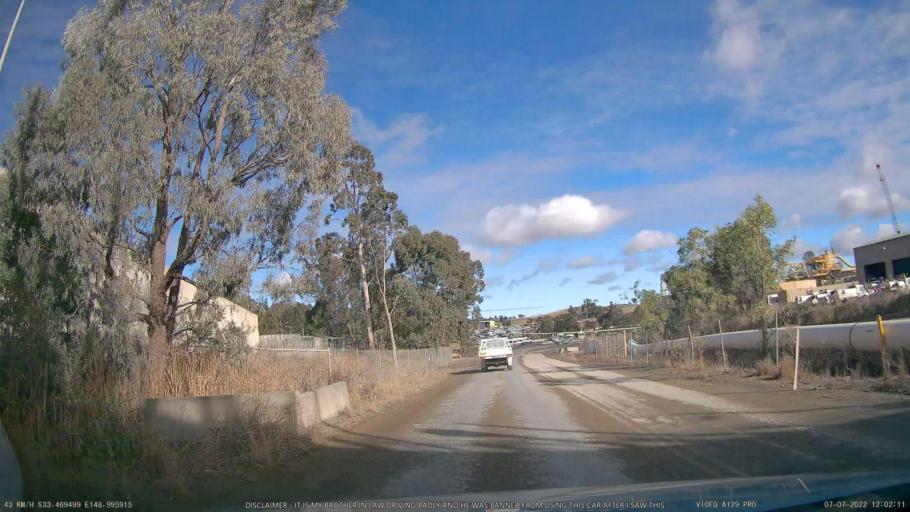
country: AU
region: New South Wales
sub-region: Blayney
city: Millthorpe
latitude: -33.4695
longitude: 148.9956
